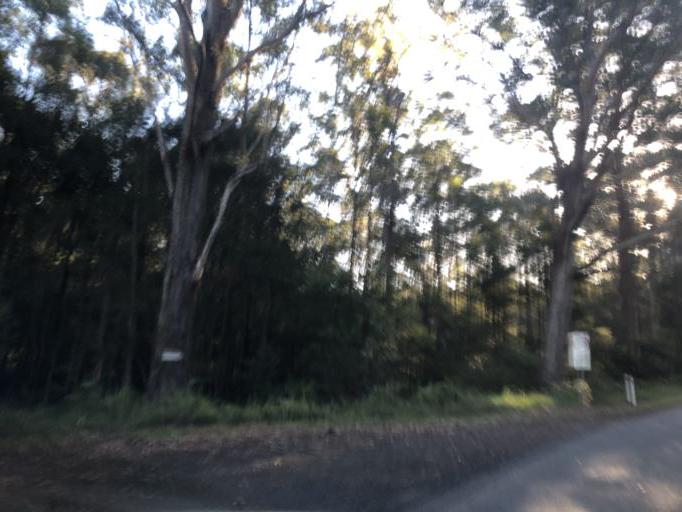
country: AU
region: New South Wales
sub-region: Nambucca Shire
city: Nambucca
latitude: -30.6108
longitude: 152.9760
